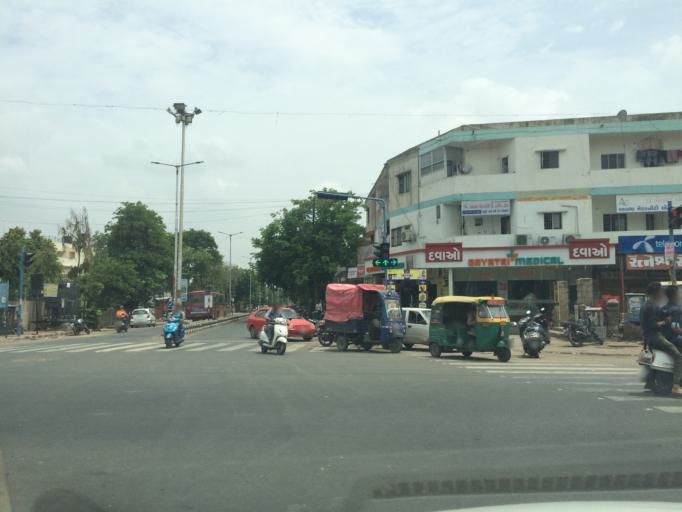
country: IN
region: Gujarat
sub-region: Ahmadabad
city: Ahmedabad
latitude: 23.0676
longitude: 72.5667
